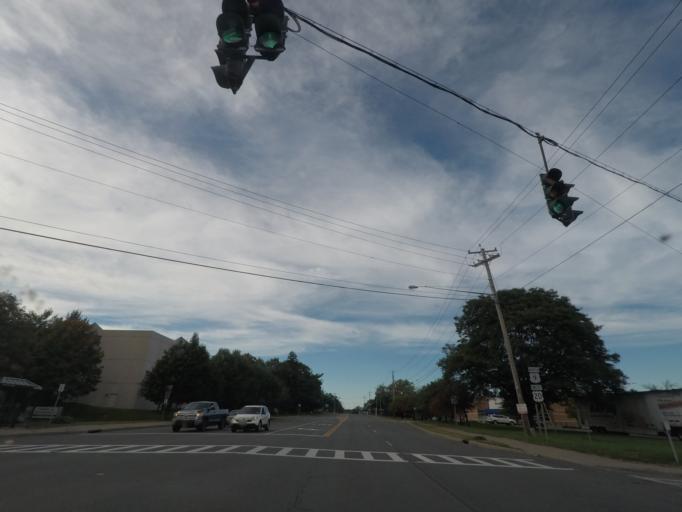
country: US
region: New York
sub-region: Rensselaer County
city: East Greenbush
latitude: 42.5651
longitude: -73.6829
